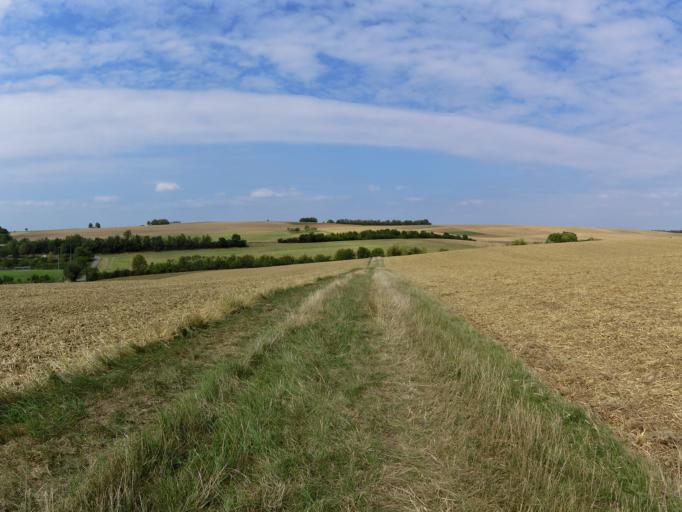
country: DE
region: Bavaria
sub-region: Regierungsbezirk Unterfranken
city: Waldbrunn
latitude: 49.7085
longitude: 9.7940
